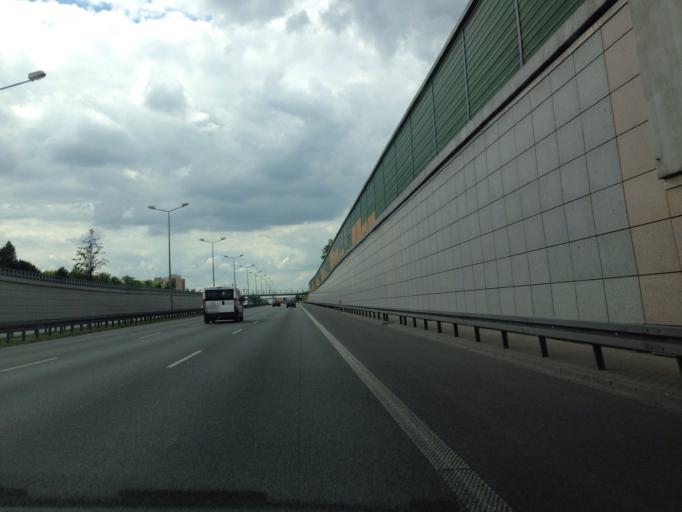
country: PL
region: Masovian Voivodeship
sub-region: Warszawa
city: Bemowo
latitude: 52.2477
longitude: 20.9231
